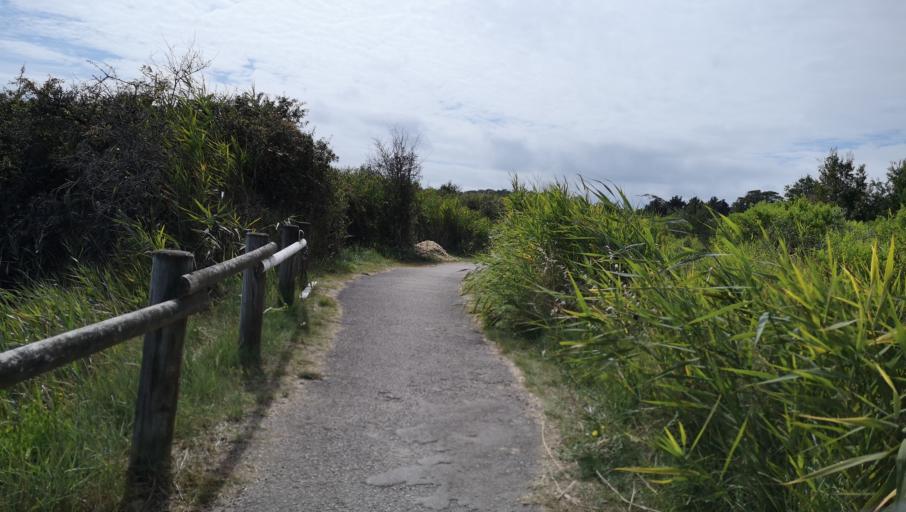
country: FR
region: Pays de la Loire
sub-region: Departement de la Vendee
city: Olonne-sur-Mer
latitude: 46.5432
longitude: -1.8041
